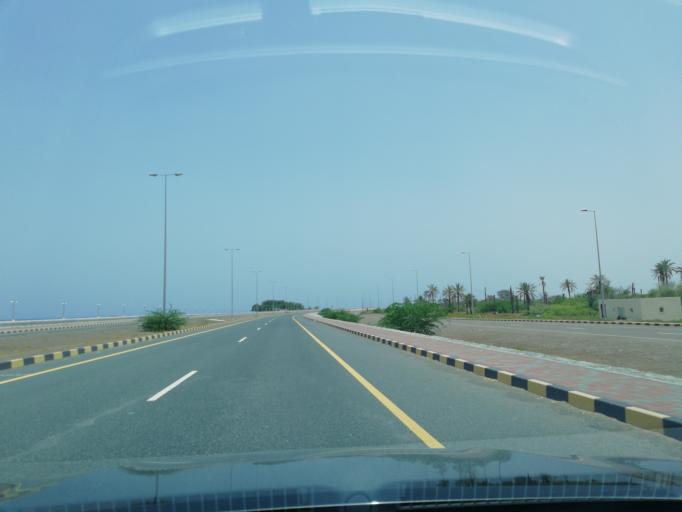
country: OM
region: Al Batinah
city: Shinas
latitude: 24.8302
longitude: 56.4330
